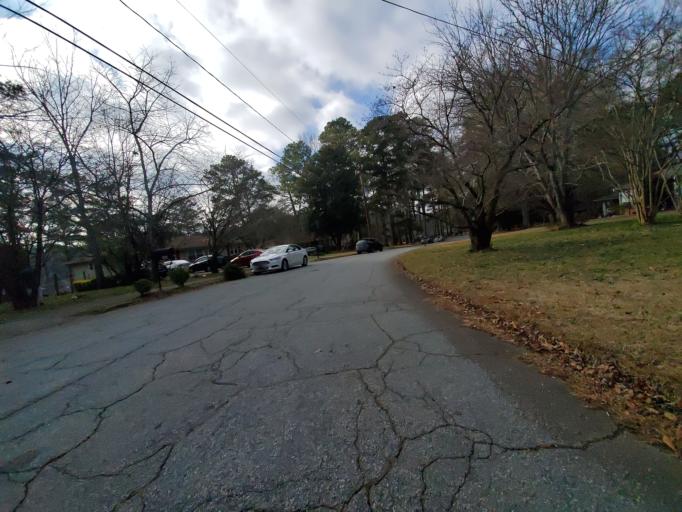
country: US
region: Georgia
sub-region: DeKalb County
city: North Decatur
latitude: 33.8035
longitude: -84.2857
